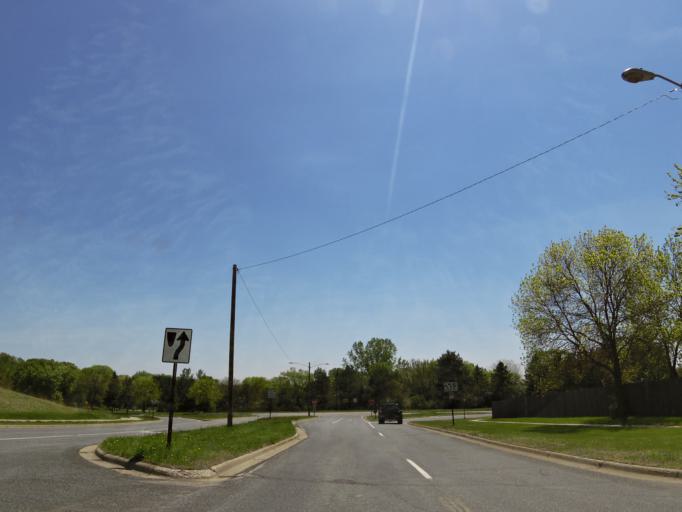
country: US
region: Minnesota
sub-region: Scott County
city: Savage
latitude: 44.8197
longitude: -93.3933
